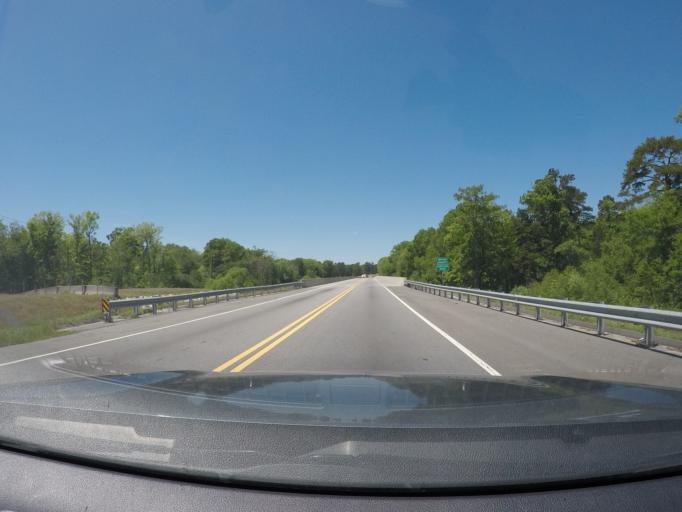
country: US
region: Georgia
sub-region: Chatham County
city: Bloomingdale
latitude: 32.1917
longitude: -81.4125
